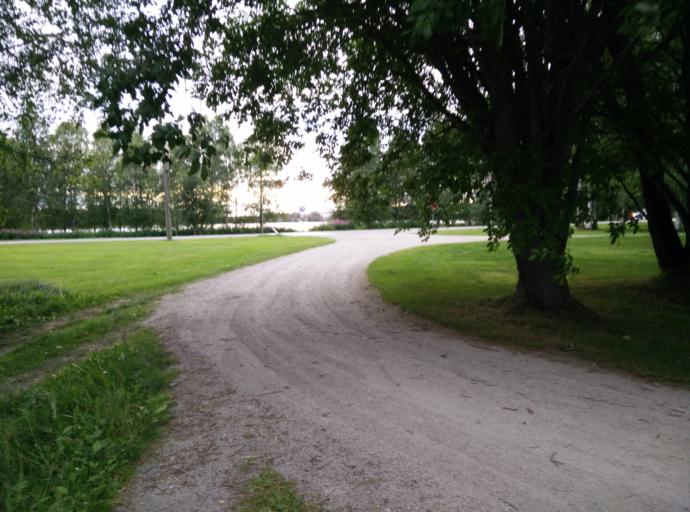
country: FI
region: Lapland
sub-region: Rovaniemi
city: Rovaniemi
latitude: 66.4885
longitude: 25.7282
